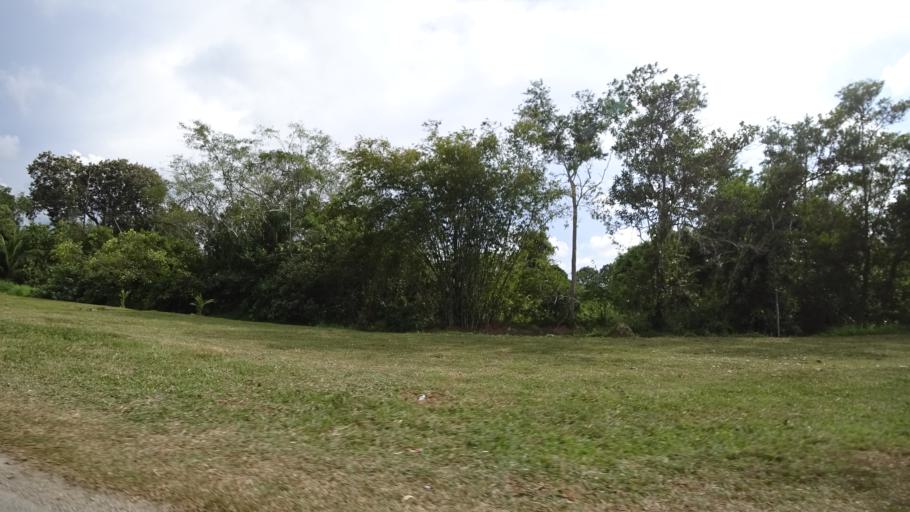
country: BN
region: Brunei and Muara
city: Bandar Seri Begawan
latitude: 4.8266
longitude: 114.8460
